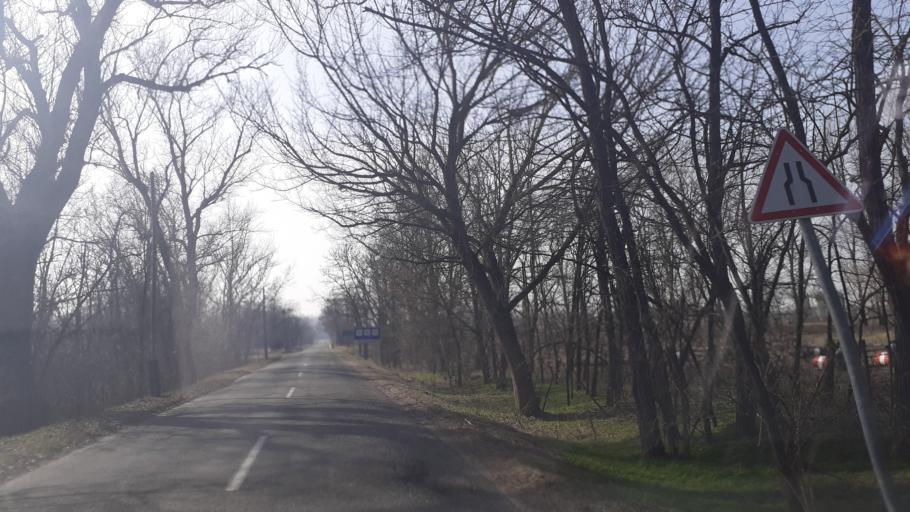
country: HU
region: Pest
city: Orkeny
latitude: 47.0530
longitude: 19.3296
